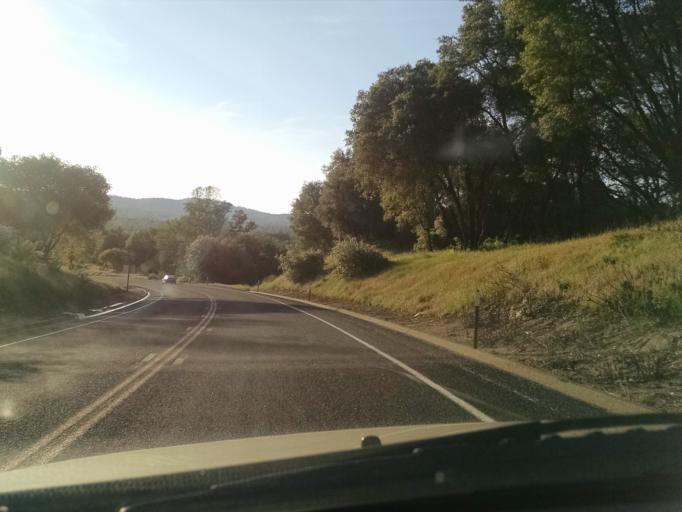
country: US
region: California
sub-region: Mariposa County
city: Midpines
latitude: 37.4591
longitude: -119.8706
